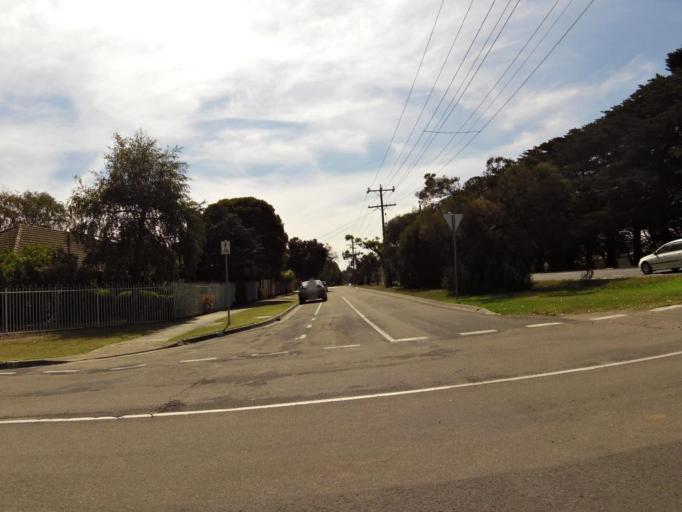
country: AU
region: Victoria
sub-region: Mornington Peninsula
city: Tyabb
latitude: -38.2323
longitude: 145.1833
